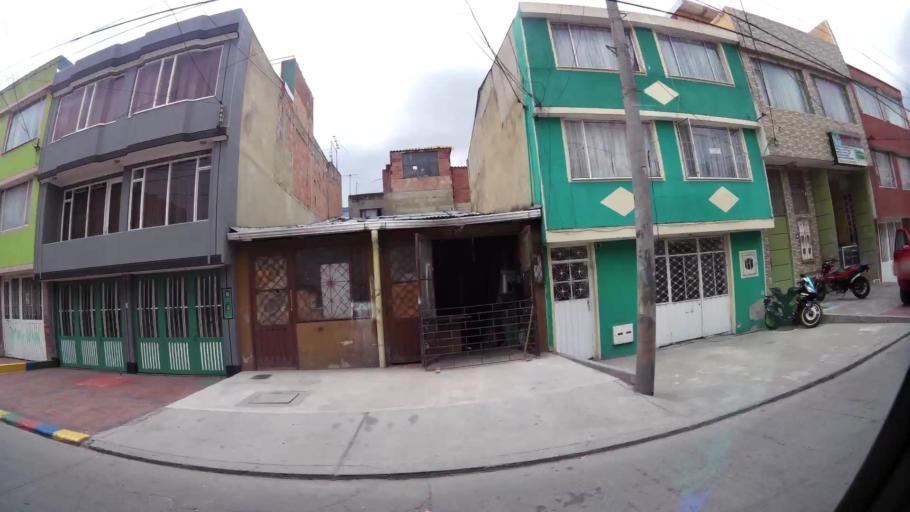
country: CO
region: Cundinamarca
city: Cota
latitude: 4.7619
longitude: -74.0382
